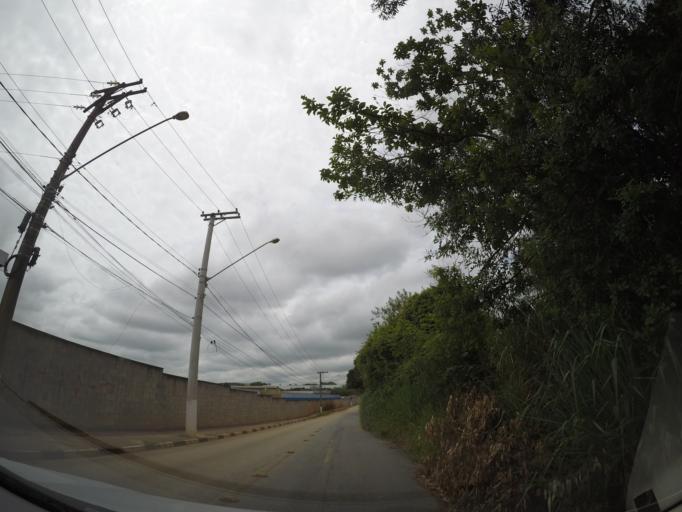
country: BR
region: Sao Paulo
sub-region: Louveira
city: Louveira
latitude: -23.0753
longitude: -46.9899
